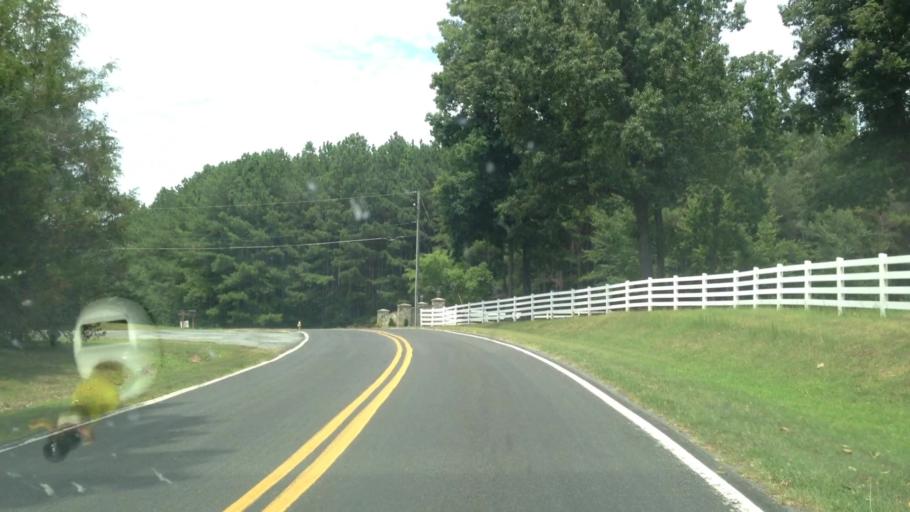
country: US
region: North Carolina
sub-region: Forsyth County
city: Walkertown
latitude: 36.1988
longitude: -80.1008
